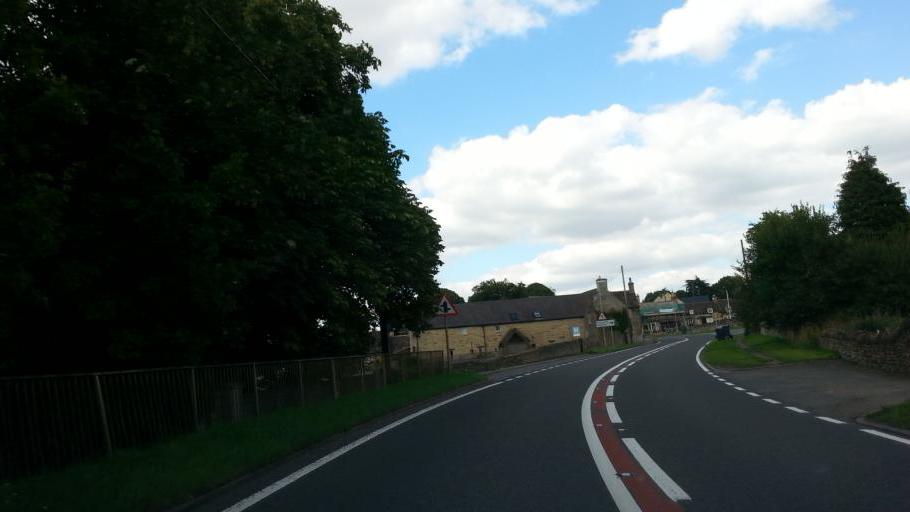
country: GB
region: England
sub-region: District of Rutland
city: Ketton
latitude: 52.6126
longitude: -0.5311
